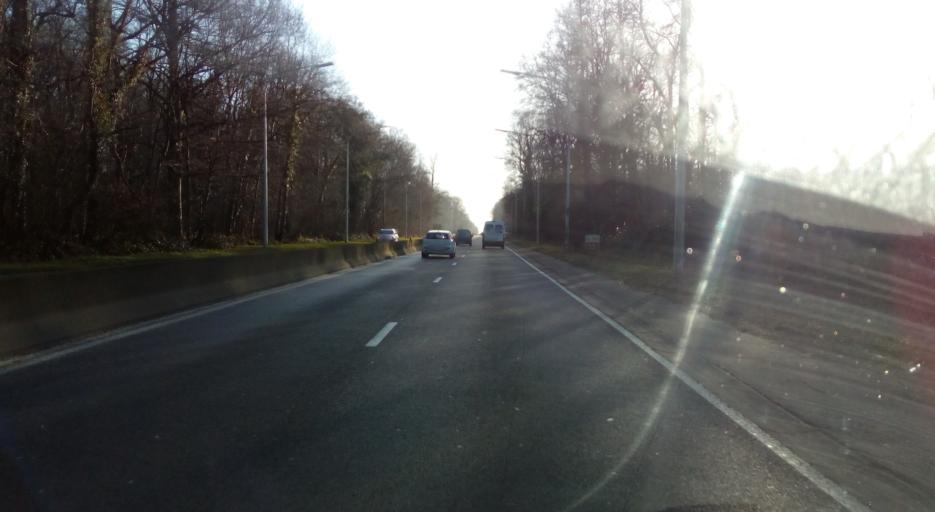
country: BE
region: Wallonia
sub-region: Province du Hainaut
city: Charleroi
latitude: 50.3579
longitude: 4.4704
